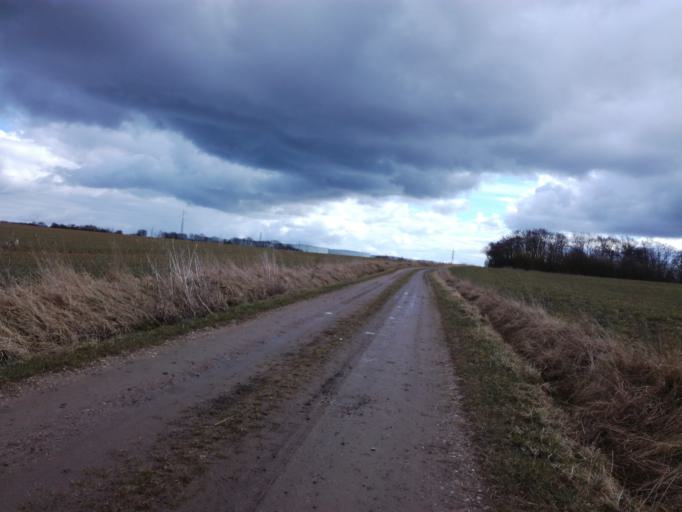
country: DK
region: South Denmark
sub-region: Fredericia Kommune
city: Fredericia
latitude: 55.6050
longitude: 9.7445
